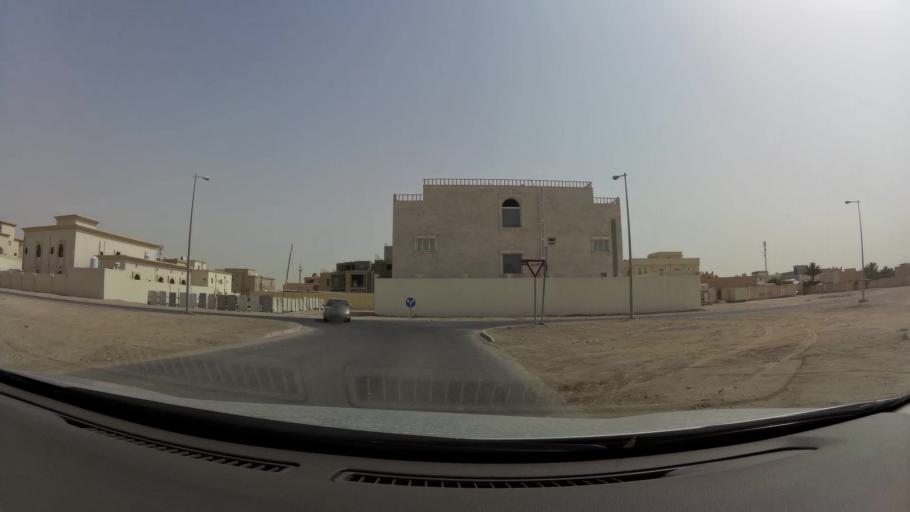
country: QA
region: Baladiyat ar Rayyan
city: Ar Rayyan
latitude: 25.2378
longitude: 51.3762
